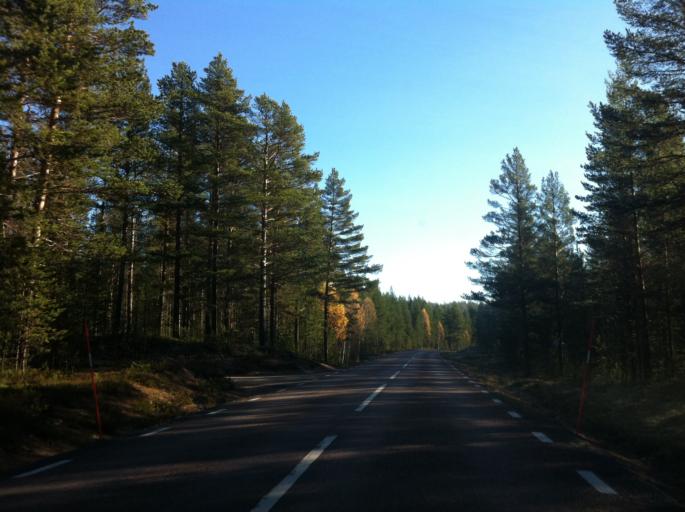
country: NO
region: Hedmark
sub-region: Trysil
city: Innbygda
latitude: 61.8426
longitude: 12.7948
